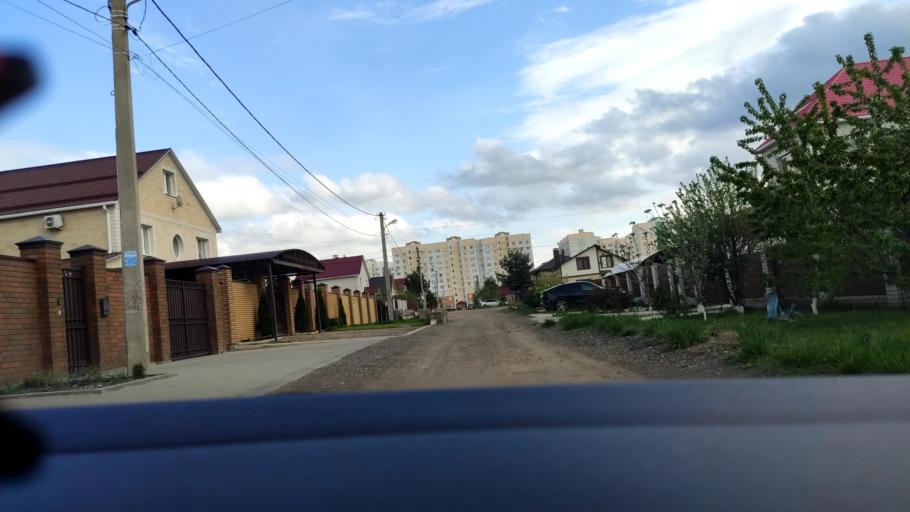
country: RU
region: Voronezj
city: Shilovo
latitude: 51.5653
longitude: 39.1106
